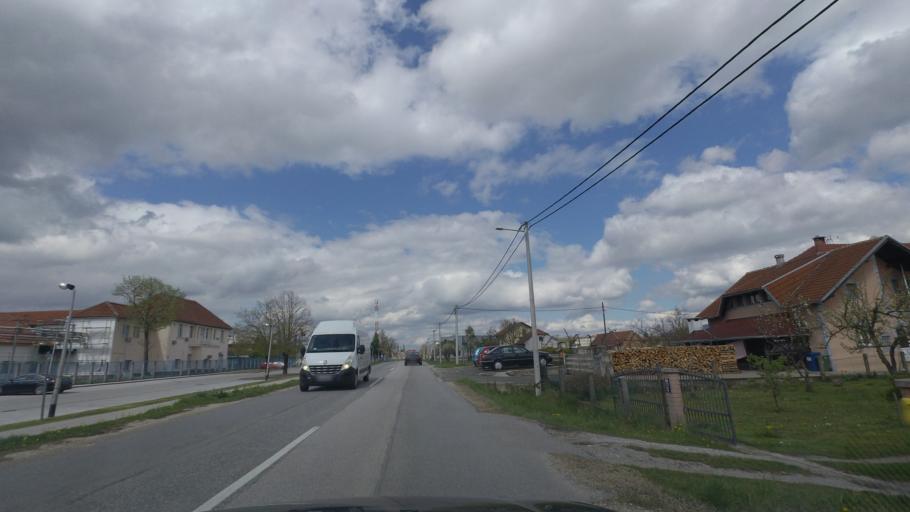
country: HR
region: Zagrebacka
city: Kerestinec
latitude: 45.7651
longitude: 15.8049
